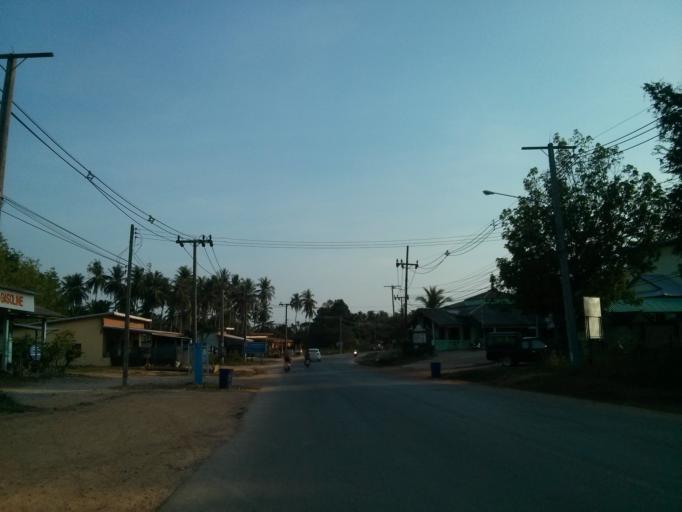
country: TH
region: Krabi
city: Saladan
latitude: 7.5847
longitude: 99.0341
